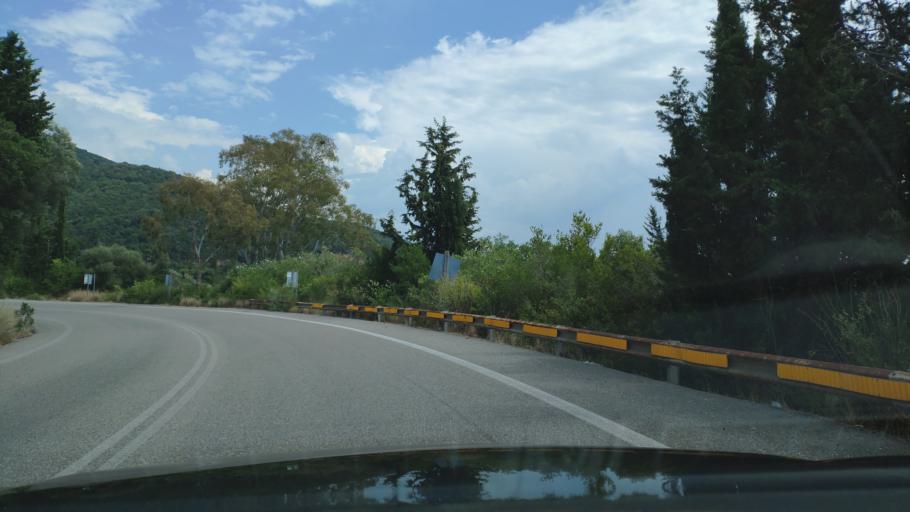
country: GR
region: West Greece
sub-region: Nomos Aitolias kai Akarnanias
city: Menidi
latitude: 39.0247
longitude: 21.1273
